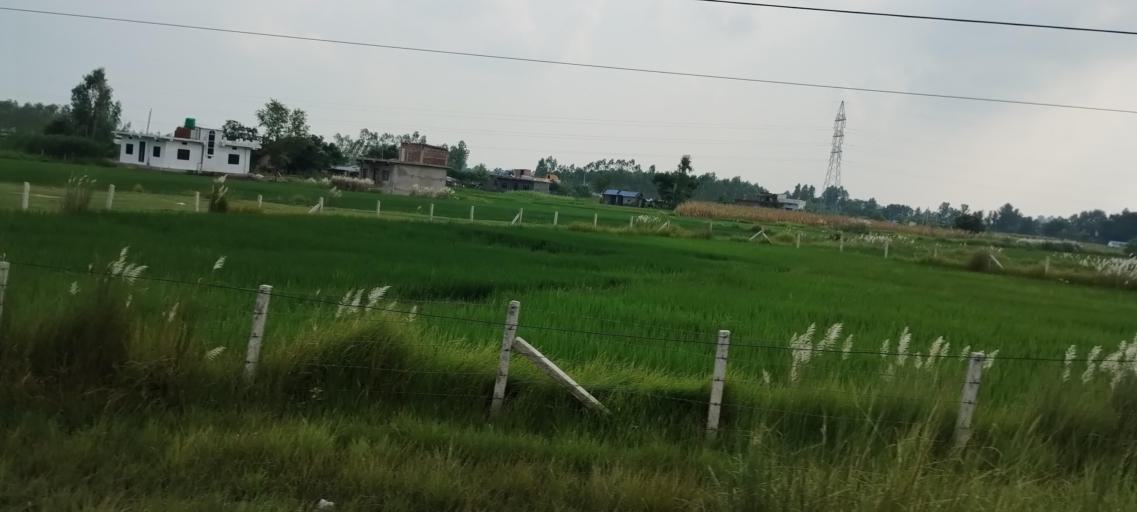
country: NP
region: Mid Western
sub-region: Bheri Zone
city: Nepalgunj
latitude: 28.1984
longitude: 81.6392
